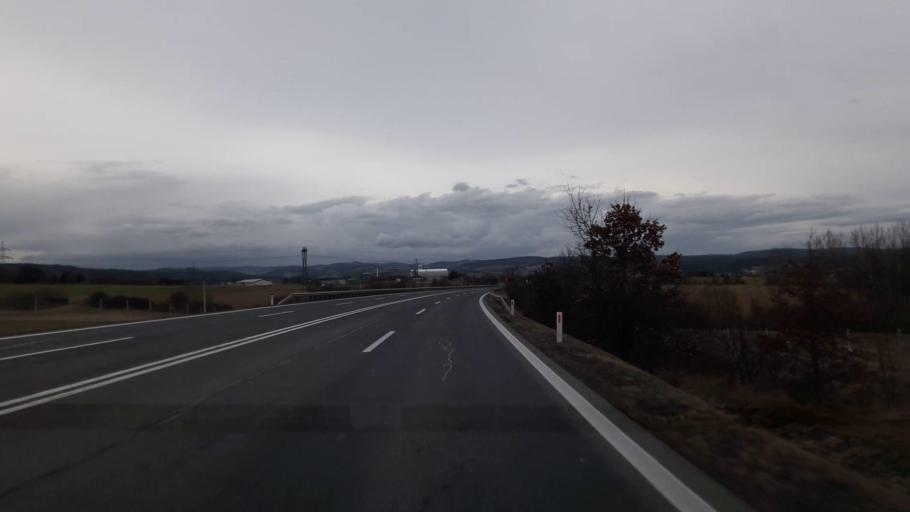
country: AT
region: Burgenland
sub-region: Politischer Bezirk Oberpullendorf
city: Markt Sankt Martin
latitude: 47.5480
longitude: 16.4193
